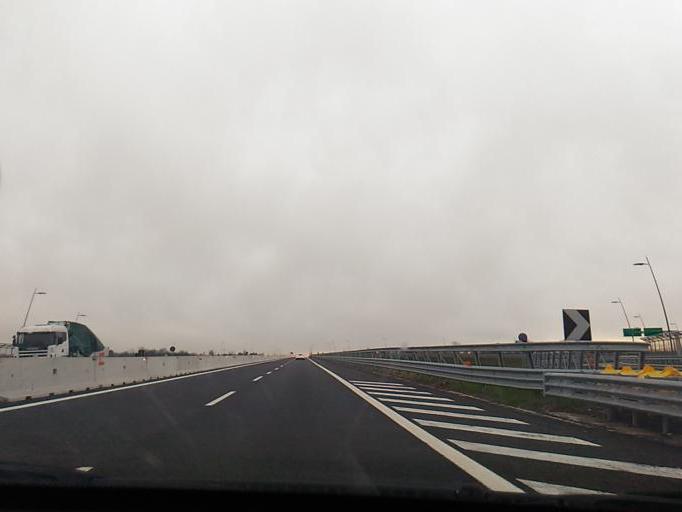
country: IT
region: Lombardy
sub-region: Provincia di Como
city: Turate
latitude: 45.6775
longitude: 9.0099
